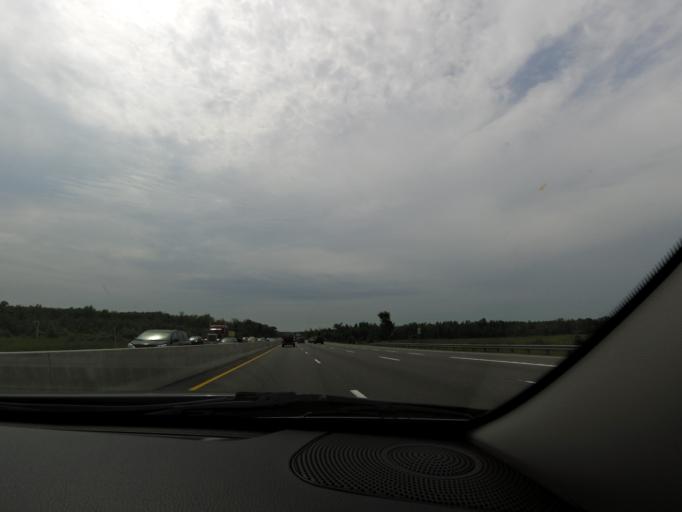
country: CA
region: Ontario
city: Bradford West Gwillimbury
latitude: 44.1971
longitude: -79.6531
